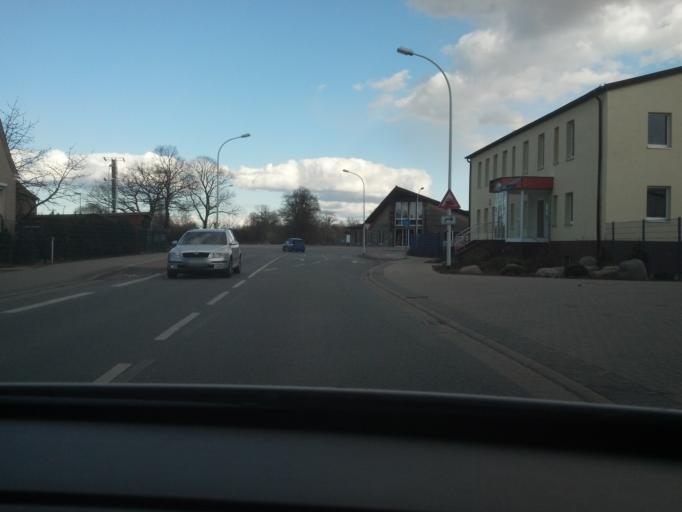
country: DE
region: Mecklenburg-Vorpommern
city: Neubrandenburg
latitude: 53.5606
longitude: 13.2814
